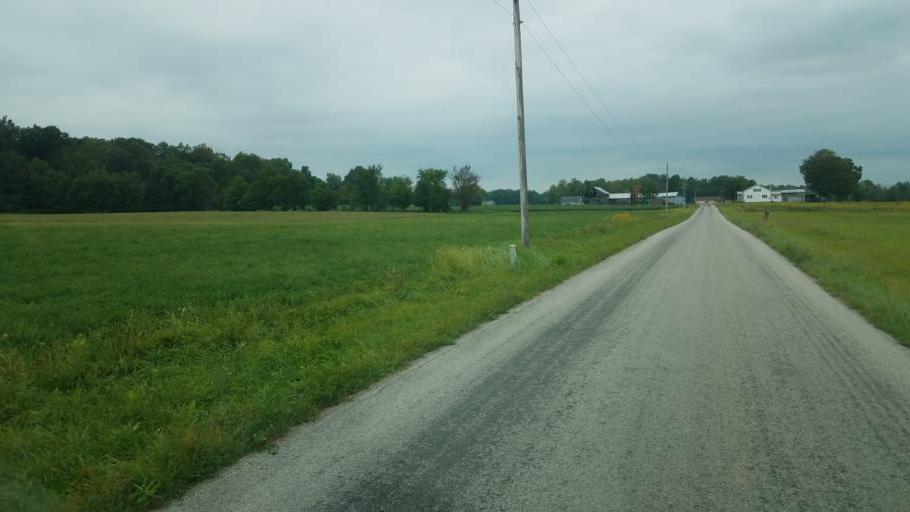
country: US
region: Ohio
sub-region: Morrow County
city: Mount Gilead
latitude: 40.5223
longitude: -82.8044
